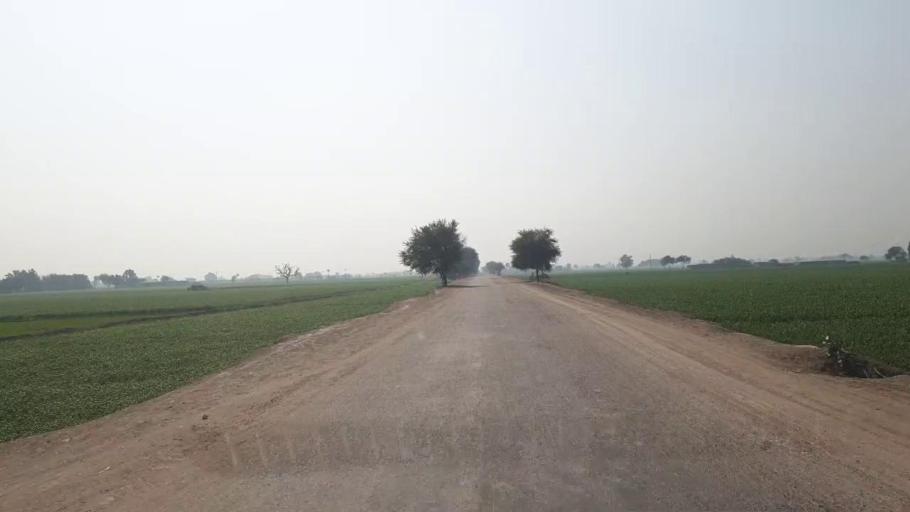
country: PK
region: Sindh
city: Hala
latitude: 25.8848
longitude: 68.4376
